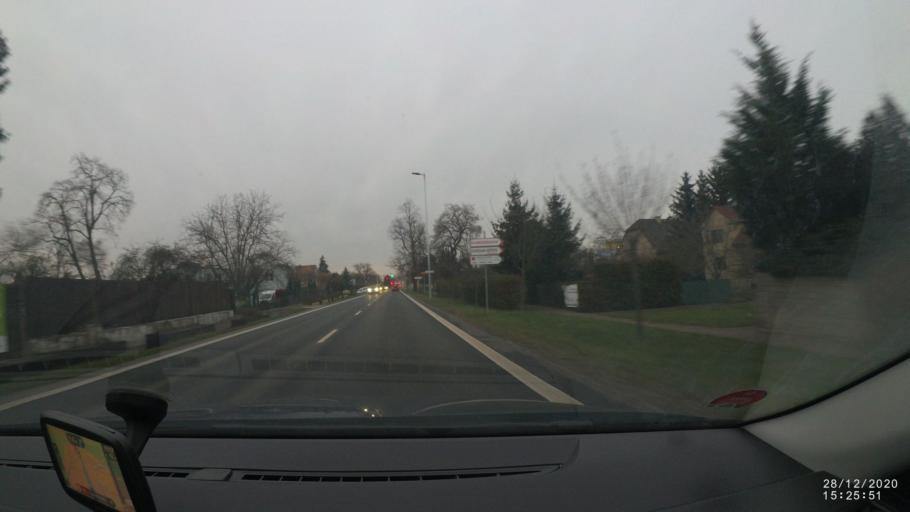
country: CZ
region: Praha
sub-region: Praha 20
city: Horni Pocernice
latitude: 50.0804
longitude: 14.6204
